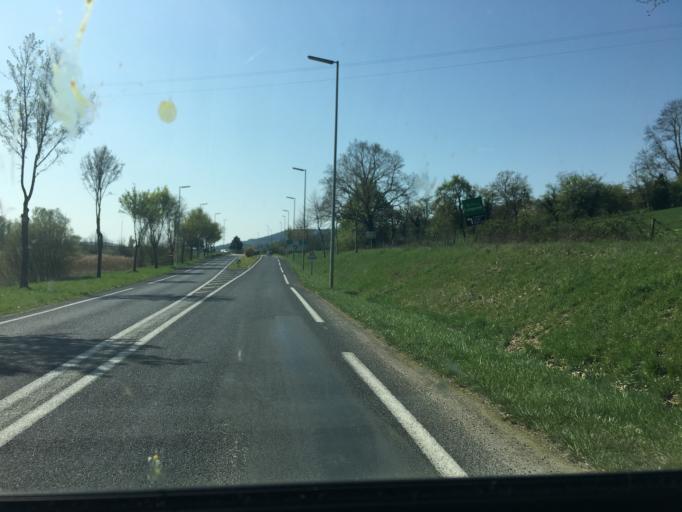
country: FR
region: Lorraine
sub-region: Departement de Meurthe-et-Moselle
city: Norroy-les-Pont-a-Mousson
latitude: 48.9195
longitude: 6.0379
